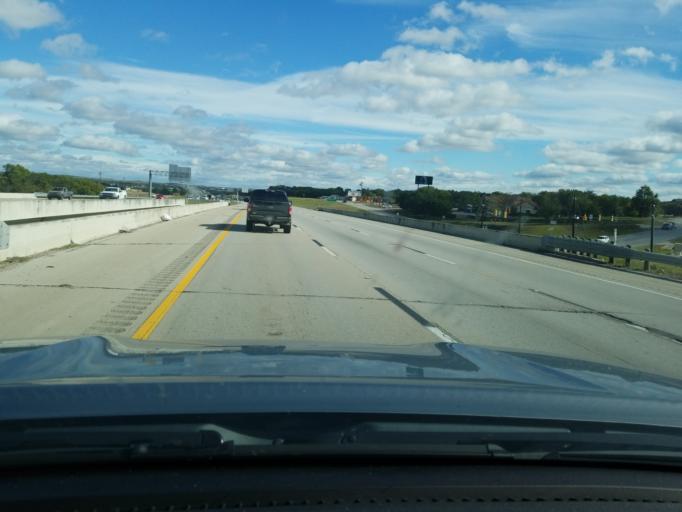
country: US
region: Texas
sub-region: Parker County
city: Willow Park
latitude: 32.7476
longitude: -97.6746
